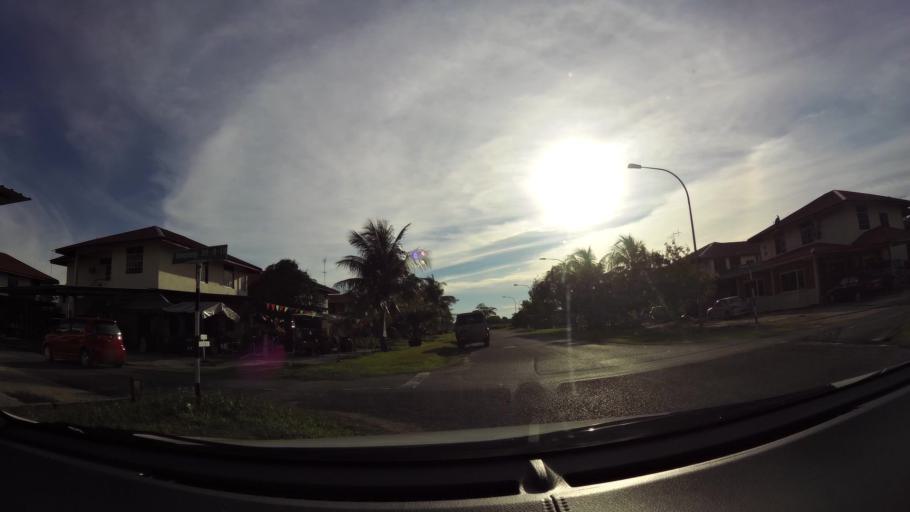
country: BN
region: Belait
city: Kuala Belait
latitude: 4.5764
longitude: 114.2220
